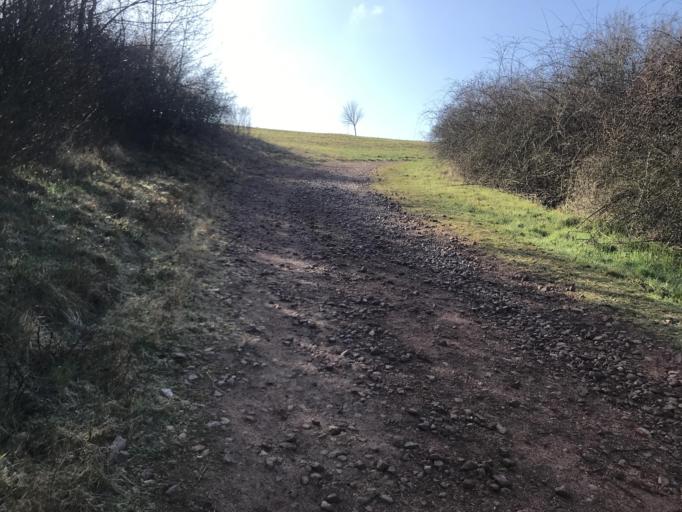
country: DE
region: Rheinland-Pfalz
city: Sankt Johann
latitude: 49.8509
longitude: 8.0077
